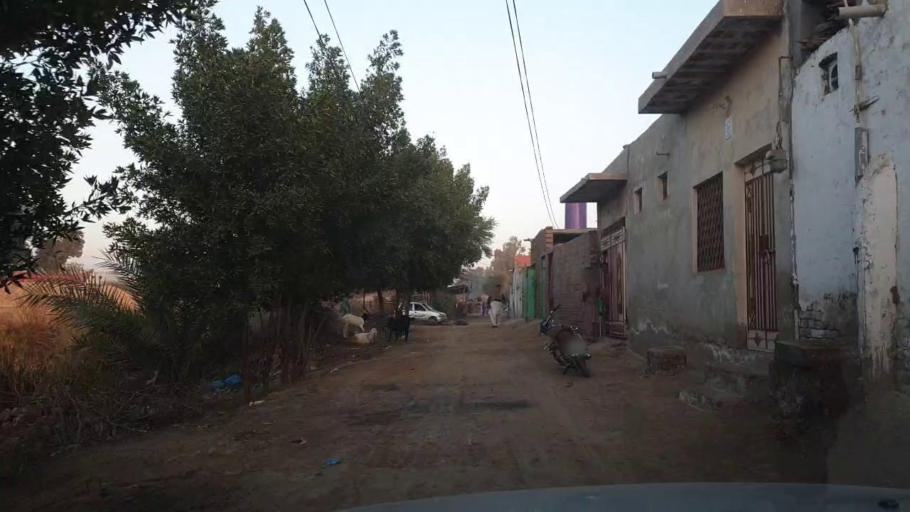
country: PK
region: Sindh
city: Mirpur Mathelo
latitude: 28.0187
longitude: 69.5537
